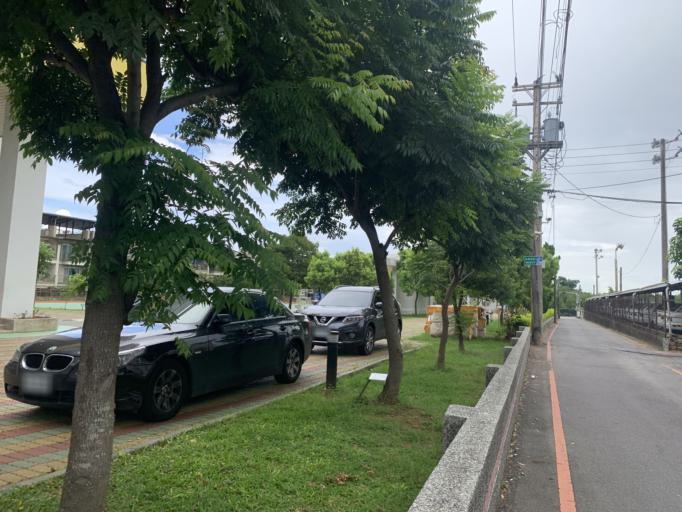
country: TW
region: Taiwan
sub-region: Chiayi
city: Jiayi Shi
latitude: 23.4916
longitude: 120.4803
